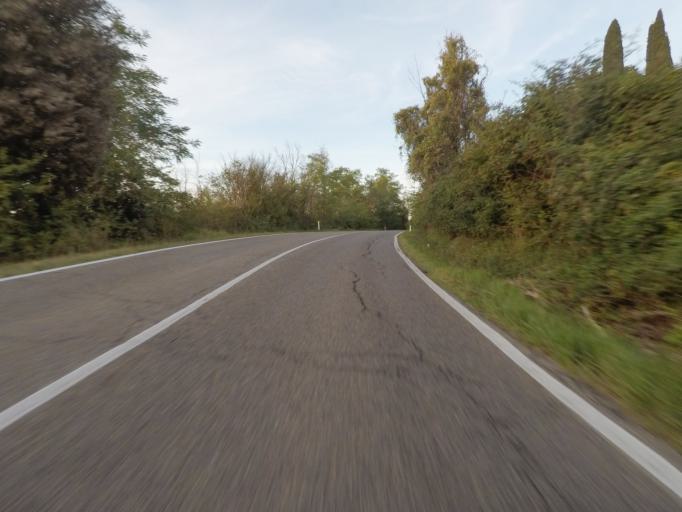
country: IT
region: Tuscany
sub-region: Provincia di Siena
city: Pienza
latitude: 43.1010
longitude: 11.6967
